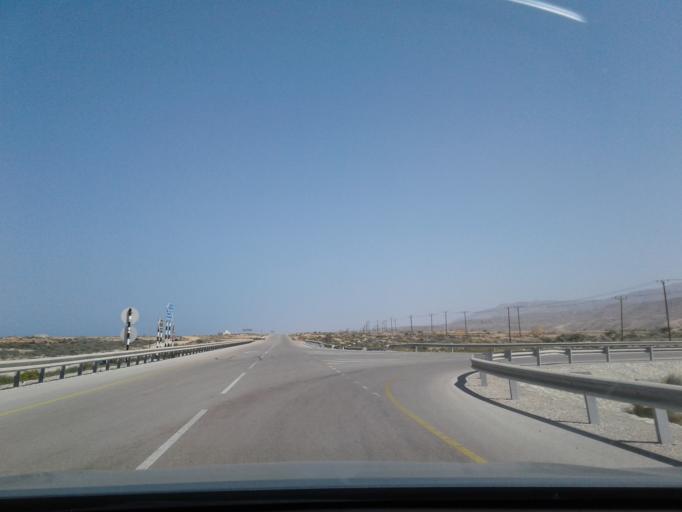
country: OM
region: Ash Sharqiyah
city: Al Qabil
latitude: 23.0321
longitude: 59.0826
